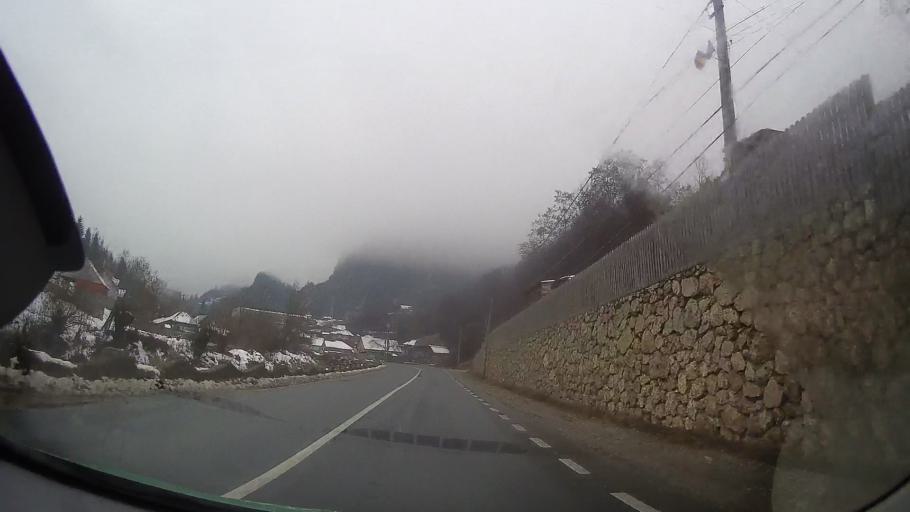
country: RO
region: Neamt
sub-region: Comuna Bicaz Chei
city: Bicaz Chei
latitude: 46.8241
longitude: 25.8612
